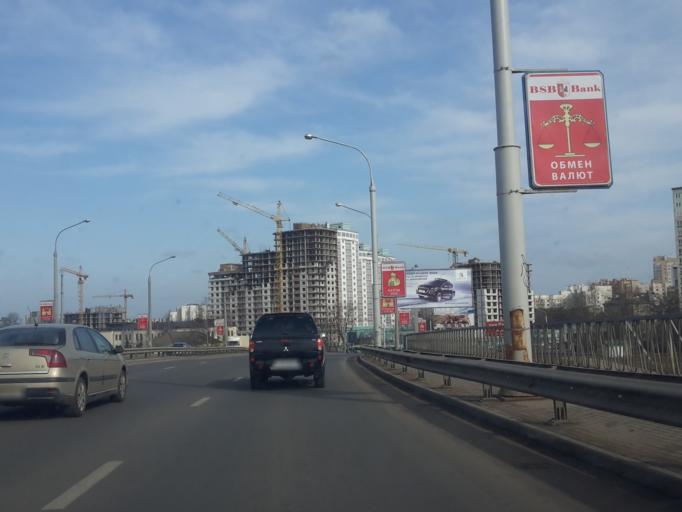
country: BY
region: Minsk
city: Minsk
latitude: 53.9093
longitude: 27.5242
